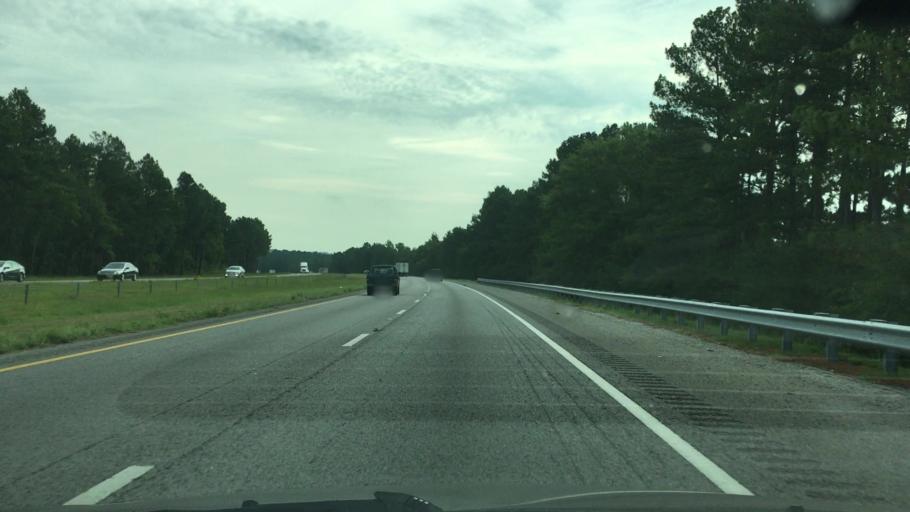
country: US
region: South Carolina
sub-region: Aiken County
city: Aiken
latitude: 33.6824
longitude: -81.6245
